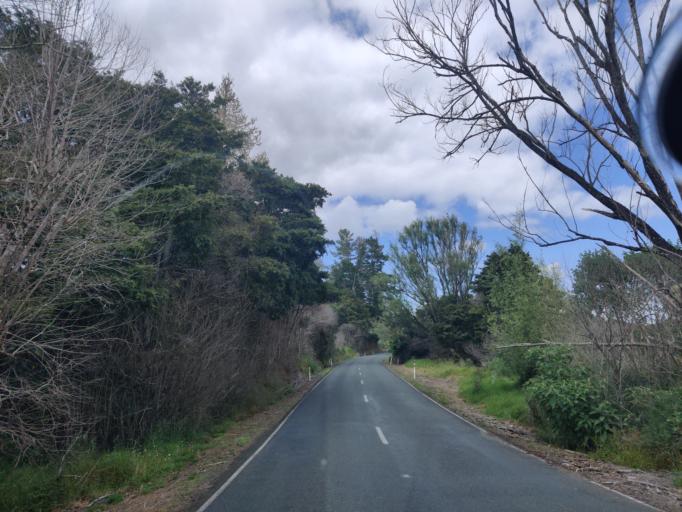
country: NZ
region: Northland
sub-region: Far North District
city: Kaitaia
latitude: -35.2802
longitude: 173.4844
